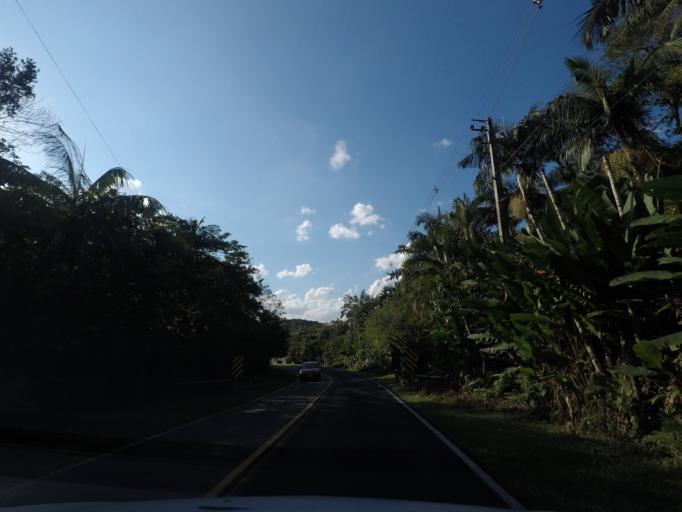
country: BR
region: Parana
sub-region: Antonina
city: Antonina
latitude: -25.4108
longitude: -48.8734
